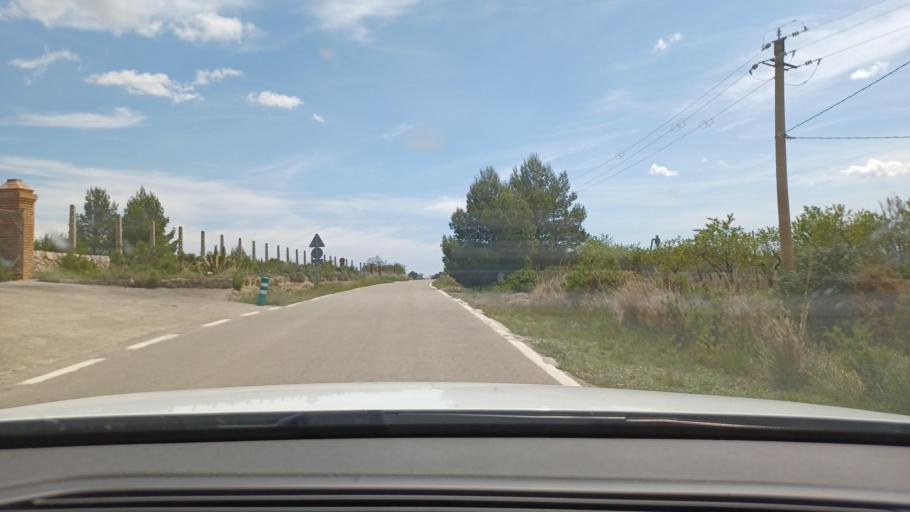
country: ES
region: Valencia
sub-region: Provincia de Castello
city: Rosell
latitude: 40.6450
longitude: 0.2723
